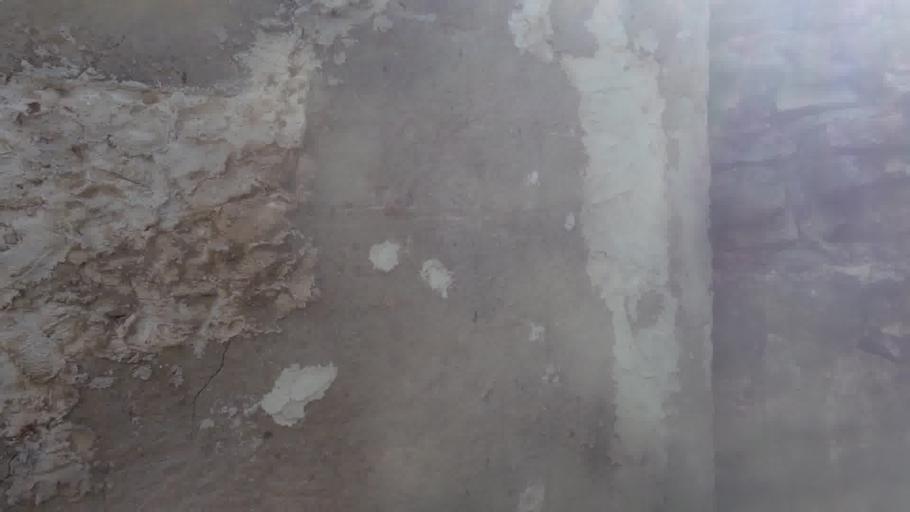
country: BR
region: Espirito Santo
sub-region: Piuma
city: Piuma
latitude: -20.8476
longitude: -40.7512
